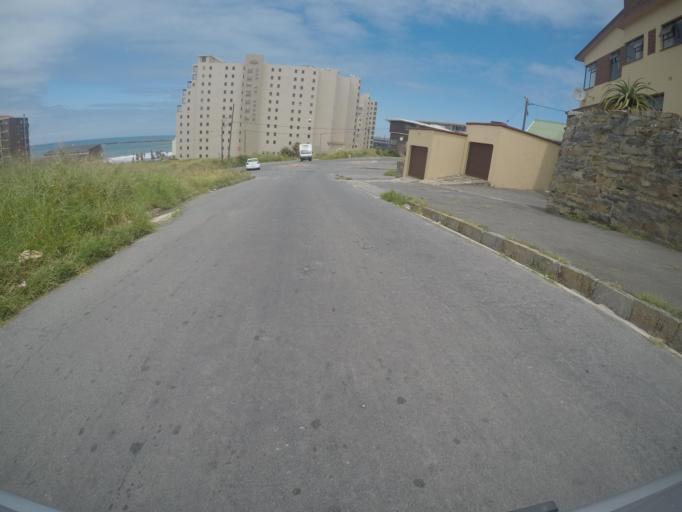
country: ZA
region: Eastern Cape
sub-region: Buffalo City Metropolitan Municipality
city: East London
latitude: -33.0169
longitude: 27.9189
